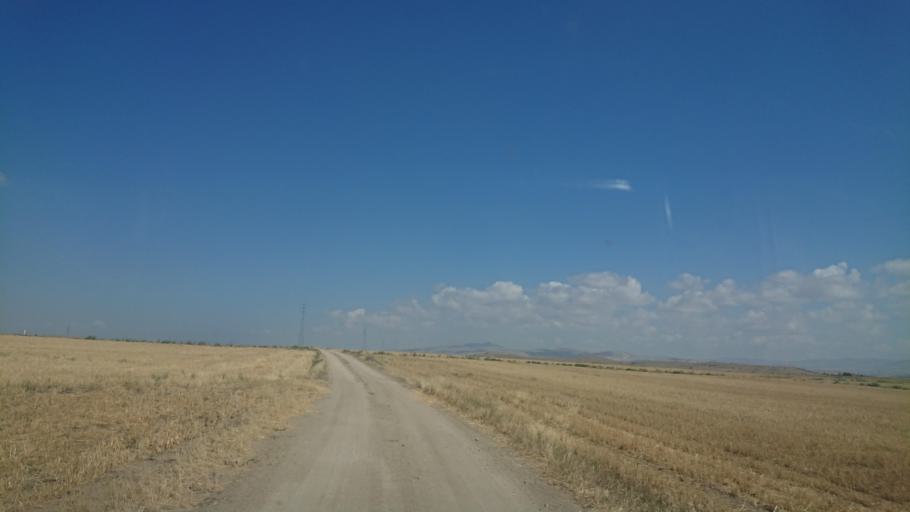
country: TR
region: Aksaray
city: Sariyahsi
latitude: 38.9991
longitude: 33.8925
